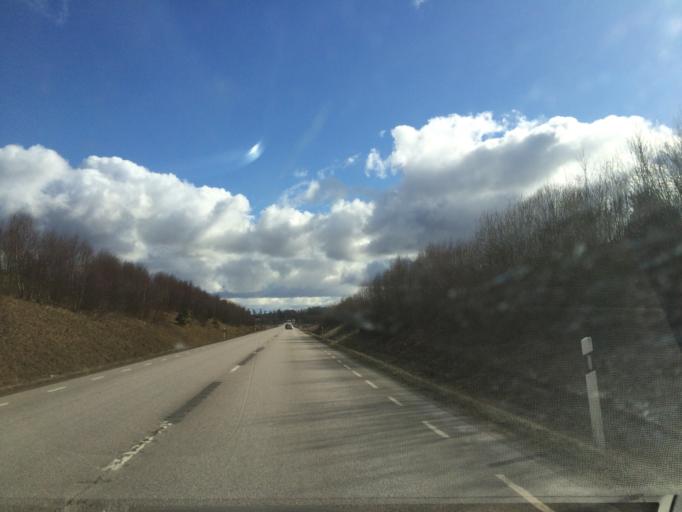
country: SE
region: Vaestra Goetaland
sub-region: Skara Kommun
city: Skara
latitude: 58.2942
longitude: 13.4732
